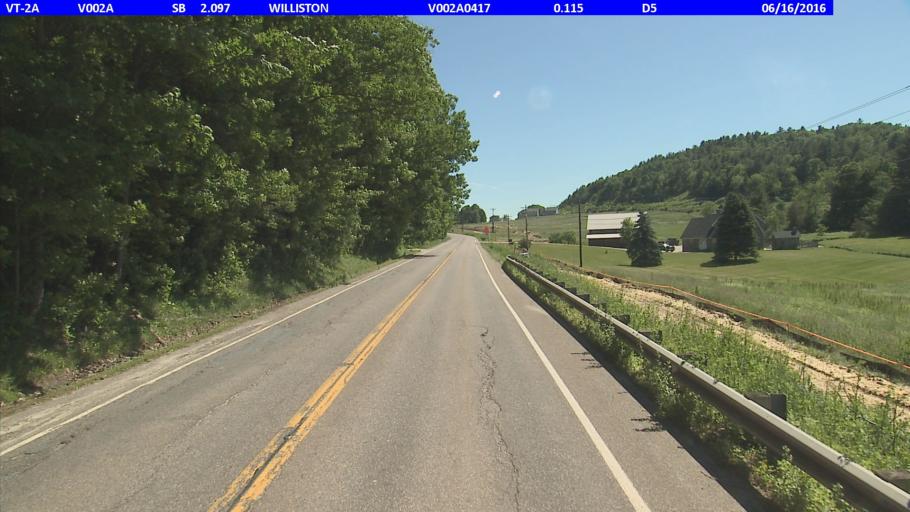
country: US
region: Vermont
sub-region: Chittenden County
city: Williston
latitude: 44.3997
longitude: -73.1277
